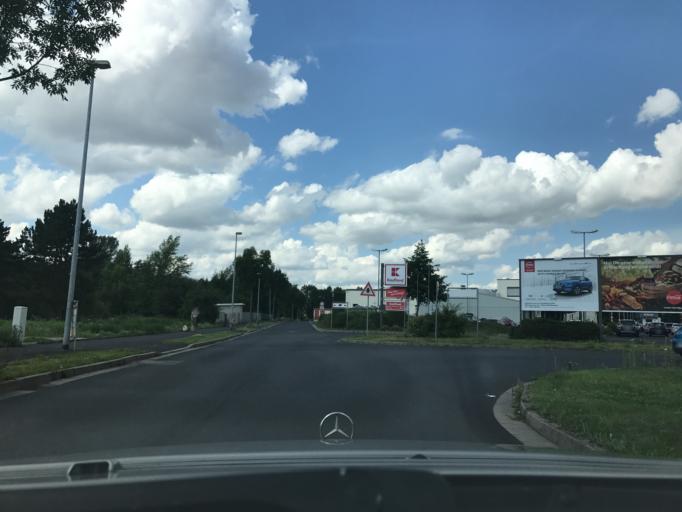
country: DE
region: Thuringia
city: Muehlhausen
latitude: 51.2225
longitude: 10.4516
